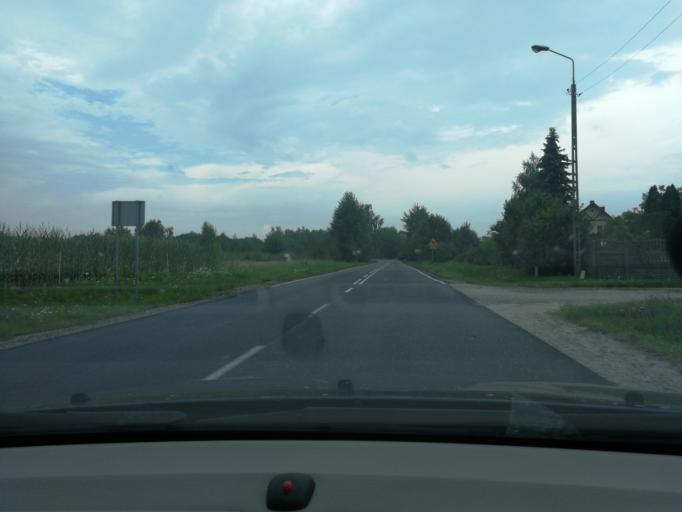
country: PL
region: Masovian Voivodeship
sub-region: Powiat zyrardowski
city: Radziejowice
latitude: 52.0103
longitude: 20.5594
